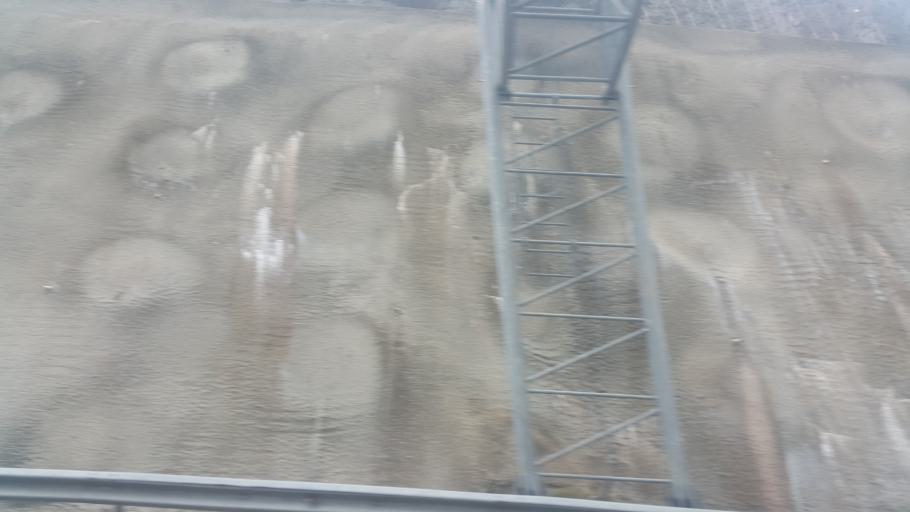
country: TR
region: Nigde
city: Ciftehan
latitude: 37.5559
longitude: 34.7687
